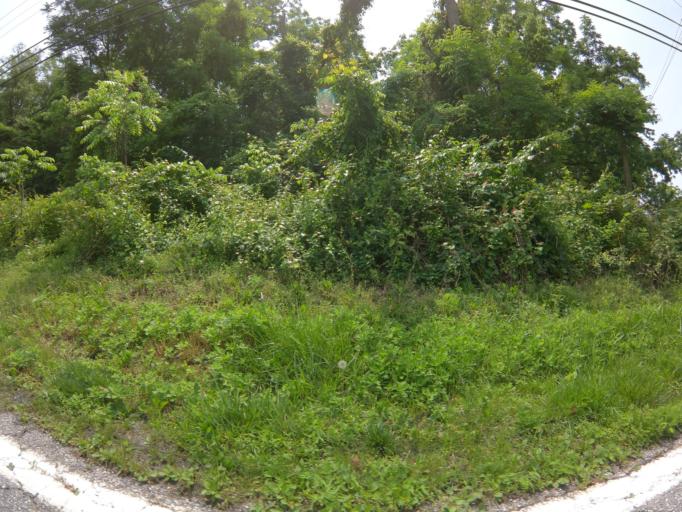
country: US
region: Maryland
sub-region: Howard County
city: Ellicott City
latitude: 39.2390
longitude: -76.8026
